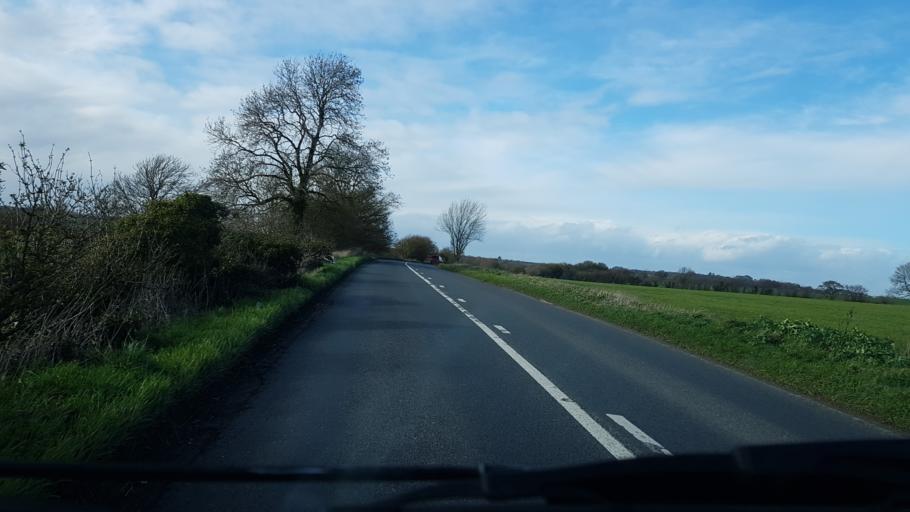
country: GB
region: England
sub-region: Wiltshire
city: Avebury
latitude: 51.4637
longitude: -1.8483
